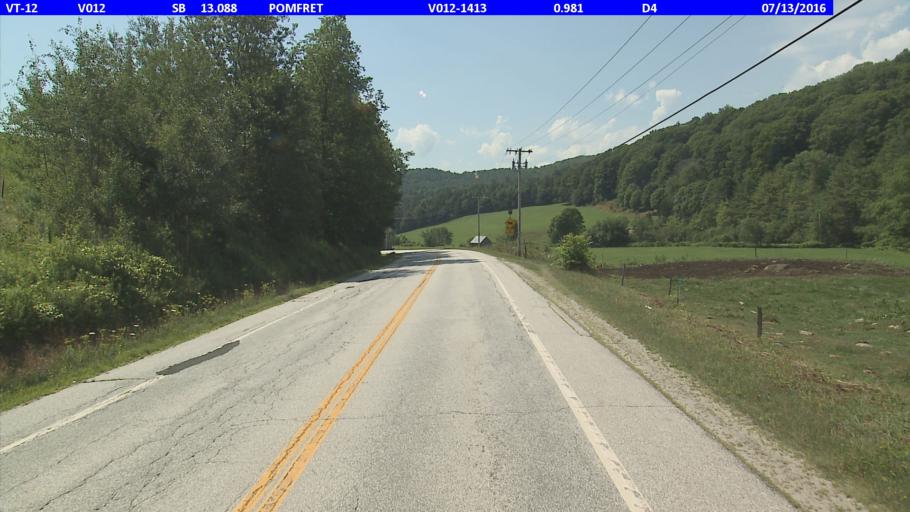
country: US
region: Vermont
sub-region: Windsor County
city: Woodstock
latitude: 43.6699
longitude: -72.5768
